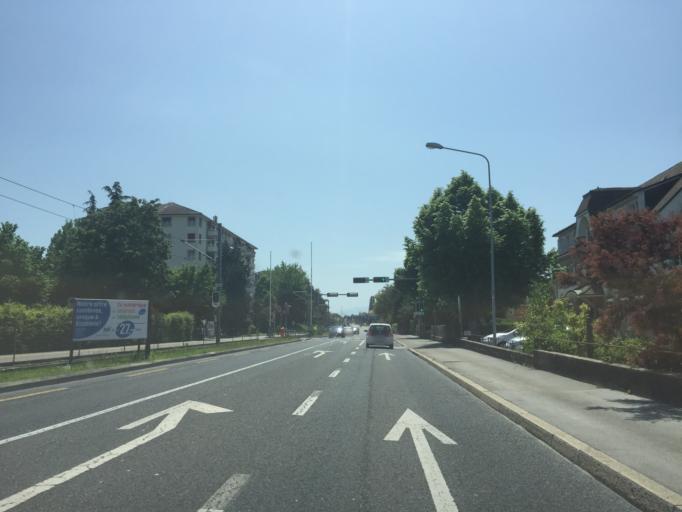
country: CH
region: Vaud
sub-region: Ouest Lausannois District
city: Chavannes
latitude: 46.5312
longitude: 6.5687
